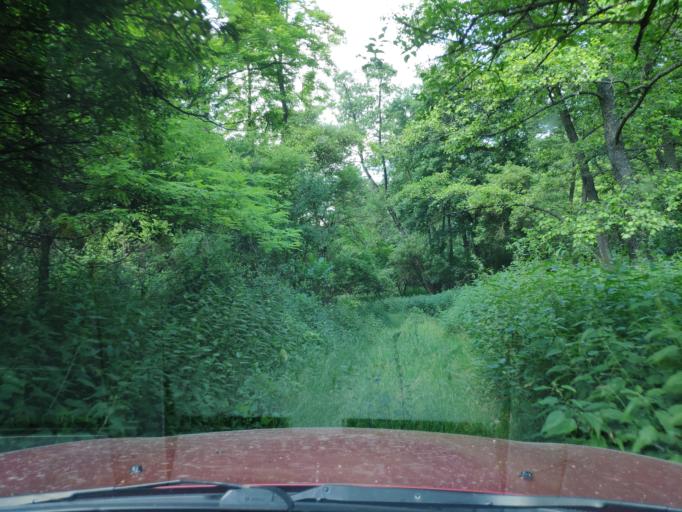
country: HU
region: Borsod-Abauj-Zemplen
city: Arlo
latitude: 48.2566
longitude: 20.1691
